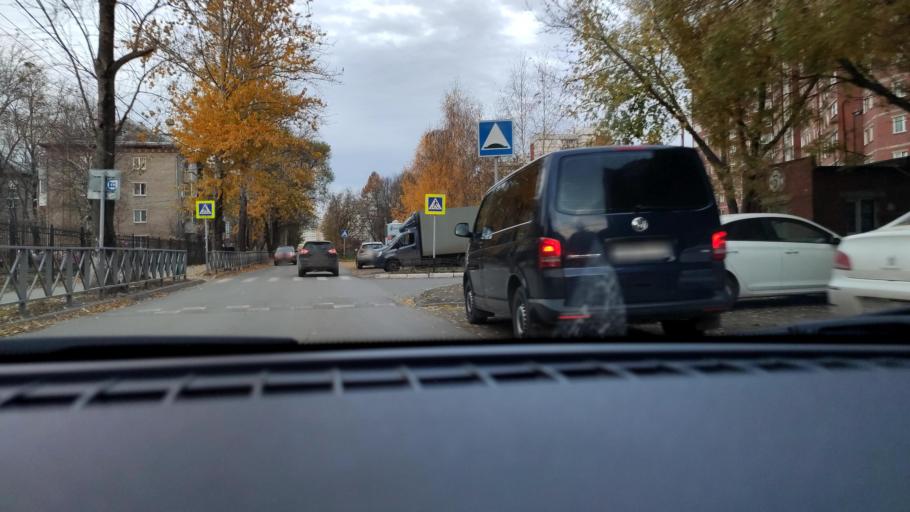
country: RU
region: Perm
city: Perm
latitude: 57.9797
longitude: 56.1986
